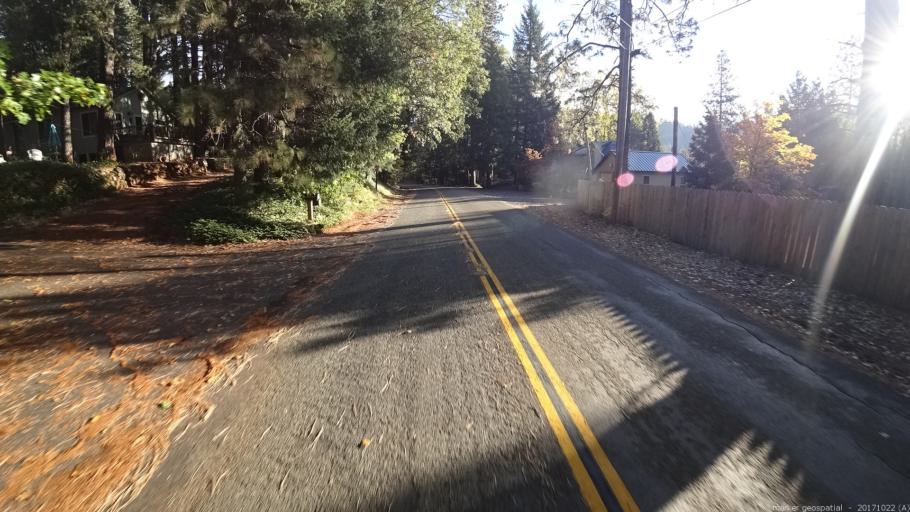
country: US
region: California
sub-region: Siskiyou County
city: Dunsmuir
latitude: 41.1759
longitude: -122.2935
